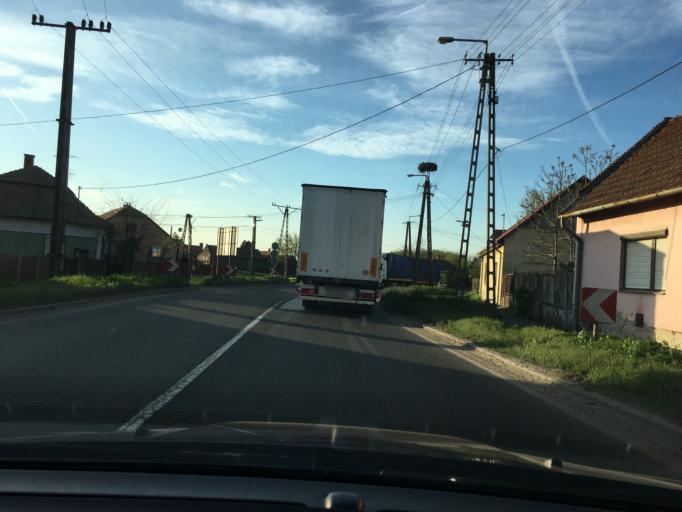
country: HU
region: Hajdu-Bihar
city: Mikepercs
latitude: 47.4426
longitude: 21.6321
